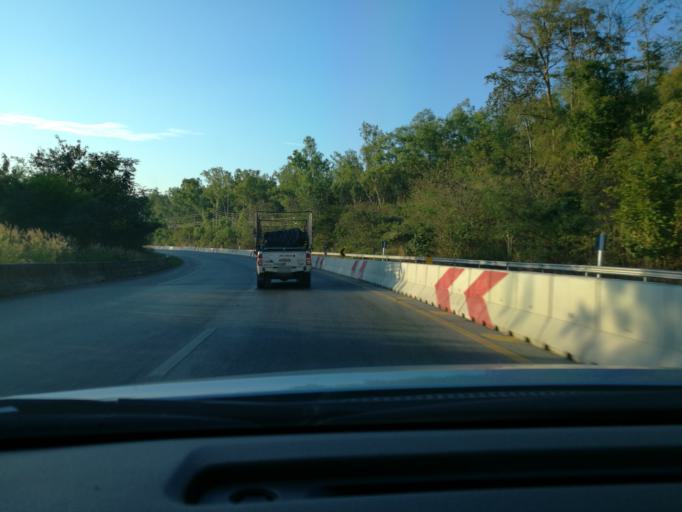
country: TH
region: Phitsanulok
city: Wang Thong
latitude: 16.8549
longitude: 100.5102
